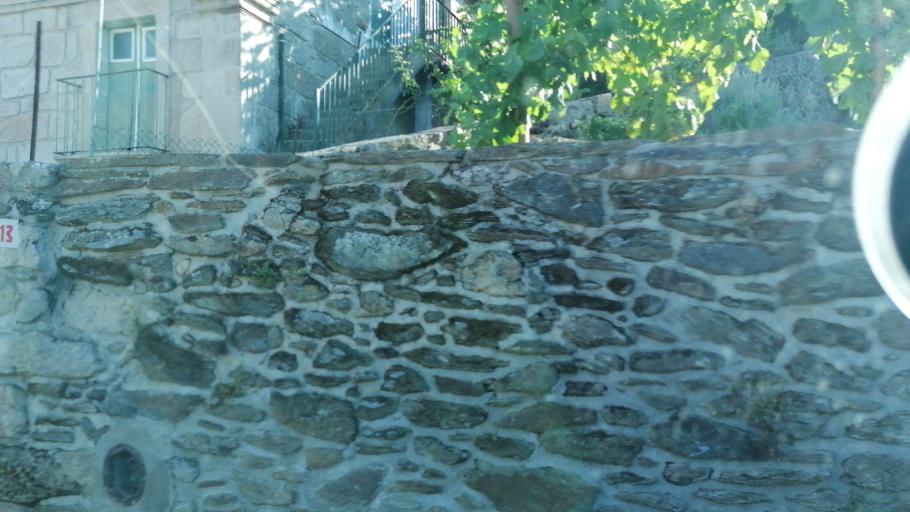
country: PT
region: Viseu
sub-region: Sao Joao da Pesqueira
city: Sao Joao da Pesqueira
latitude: 41.2480
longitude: -7.4326
